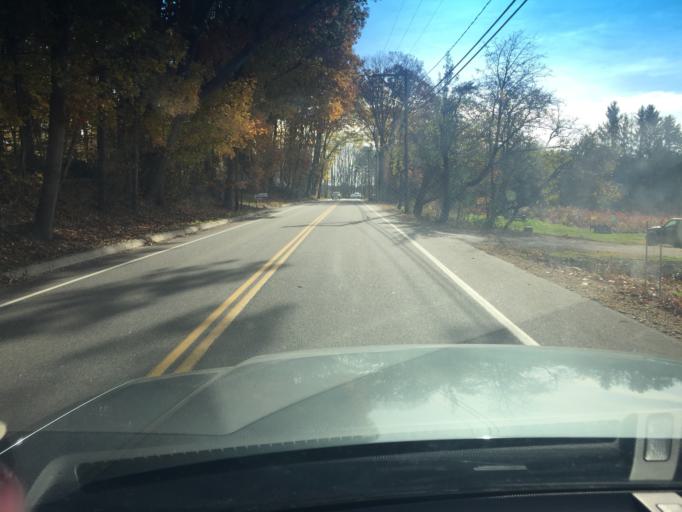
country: US
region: Maine
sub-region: York County
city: York Harbor
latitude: 43.1577
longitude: -70.6940
